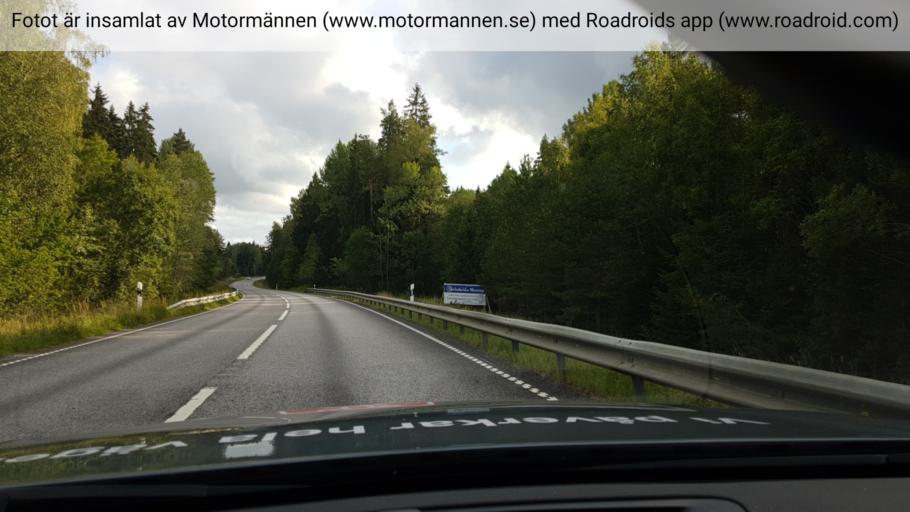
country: SE
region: Stockholm
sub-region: Norrtalje Kommun
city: Hallstavik
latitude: 59.9754
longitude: 18.5992
